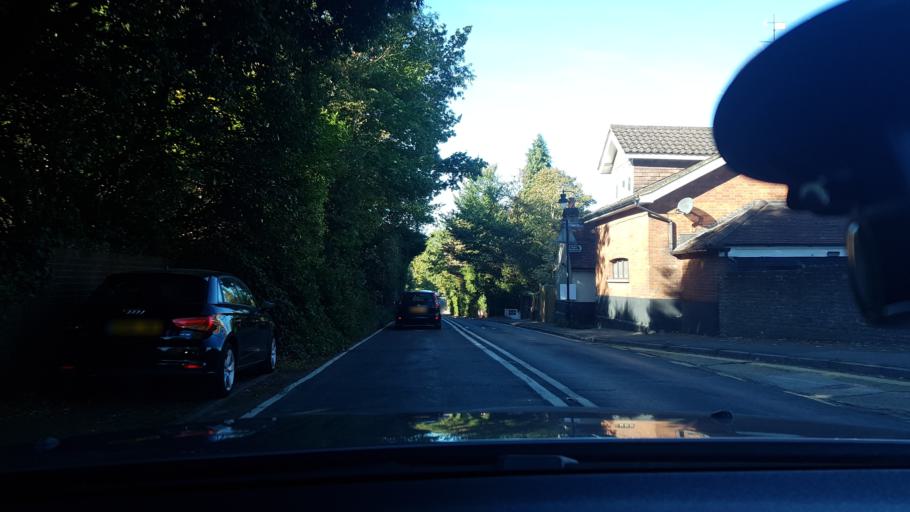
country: GB
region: England
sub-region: Surrey
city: Dorking
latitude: 51.2261
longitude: -0.3604
